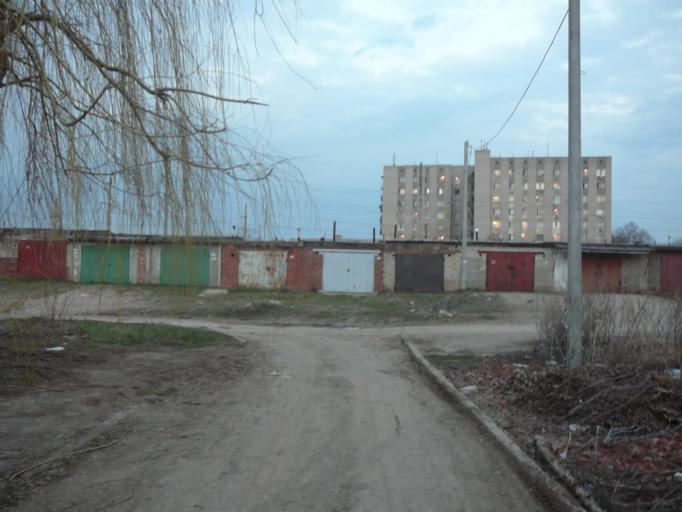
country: RU
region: Saratov
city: Engel's
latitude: 51.4735
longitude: 46.1573
